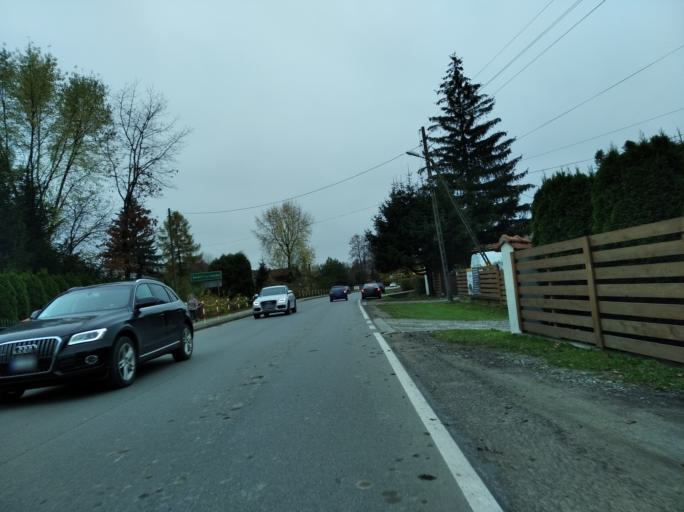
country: PL
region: Subcarpathian Voivodeship
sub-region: Powiat krosnienski
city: Chorkowka
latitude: 49.6701
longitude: 21.6935
